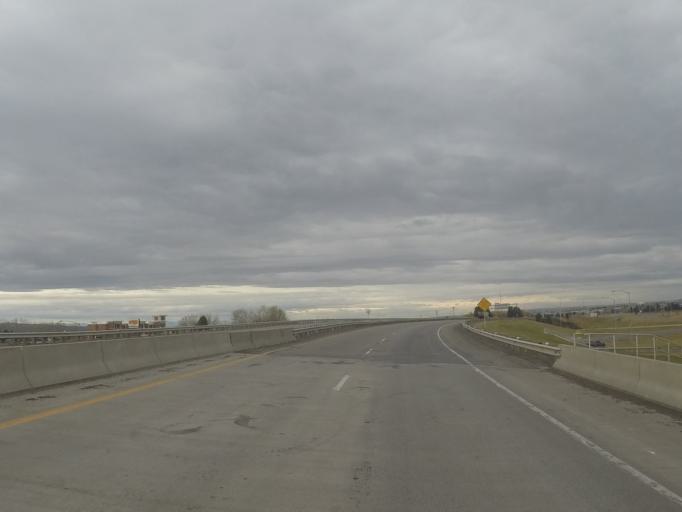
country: US
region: Montana
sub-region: Yellowstone County
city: Billings
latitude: 45.7498
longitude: -108.5565
